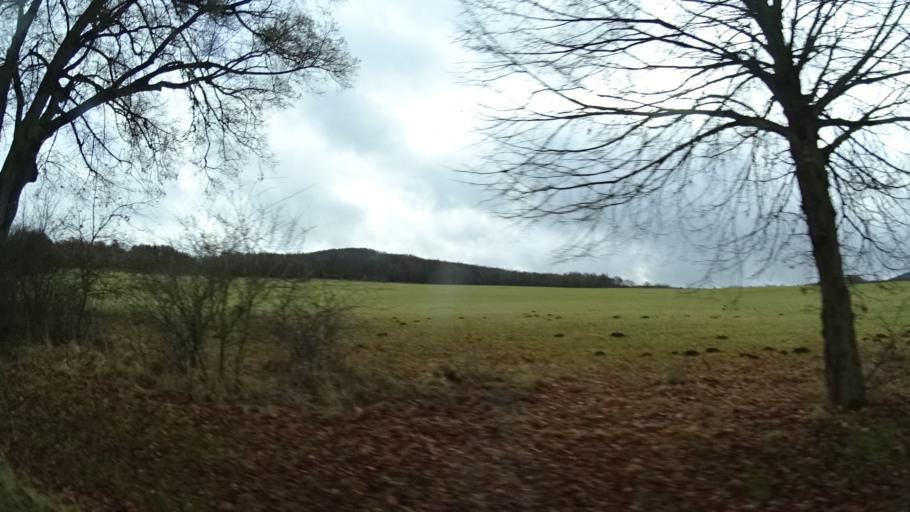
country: DE
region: Thuringia
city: Unterweid
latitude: 50.6128
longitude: 10.0444
